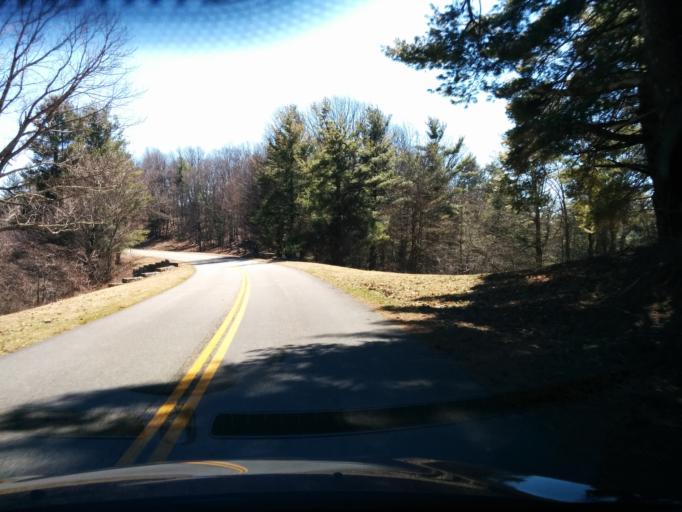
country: US
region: Virginia
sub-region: Augusta County
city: Stuarts Draft
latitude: 37.8638
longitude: -79.1487
